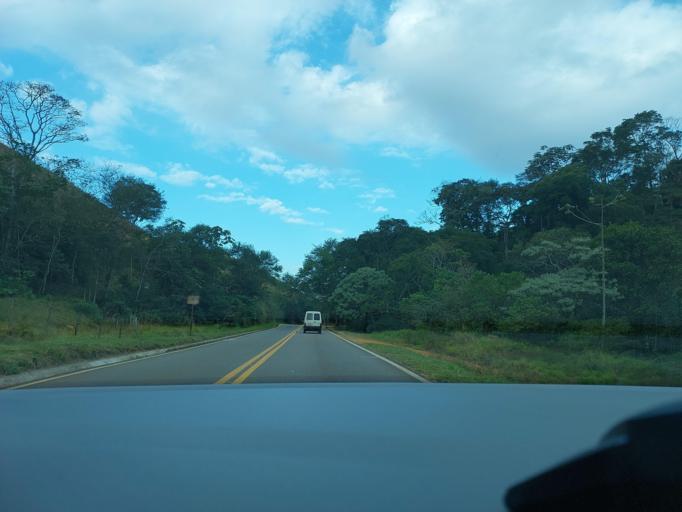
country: BR
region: Minas Gerais
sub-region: Mirai
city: Mirai
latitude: -21.0379
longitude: -42.5351
